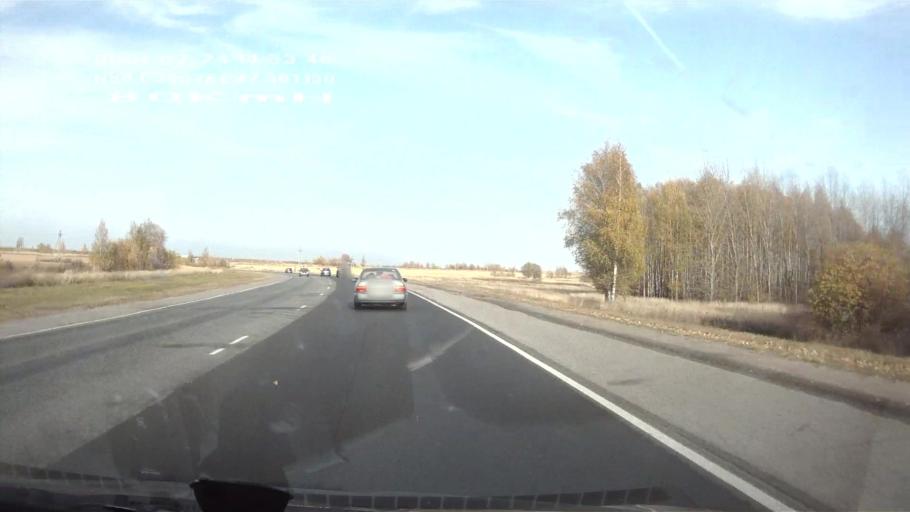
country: RU
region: Chuvashia
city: Kugesi
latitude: 56.0386
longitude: 47.3607
